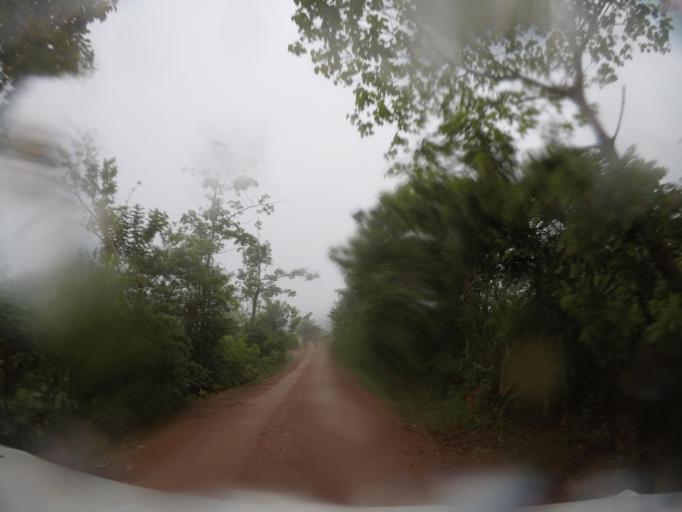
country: TL
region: Baucau
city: Venilale
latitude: -8.6344
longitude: 126.4209
